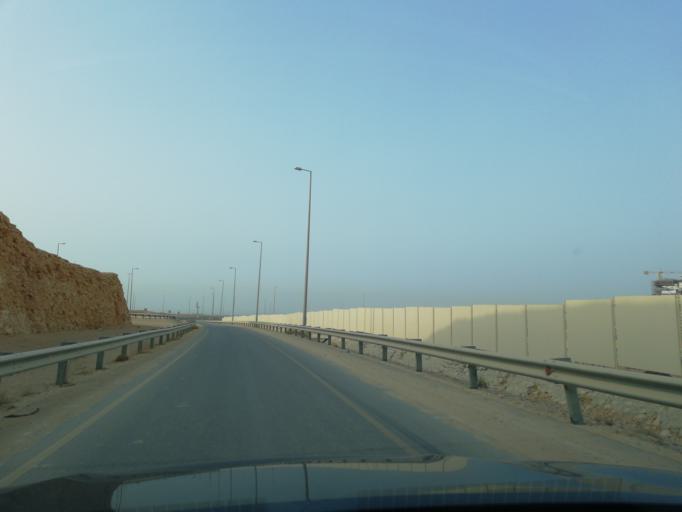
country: OM
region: Muhafazat Masqat
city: Bawshar
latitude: 23.5498
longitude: 58.2938
